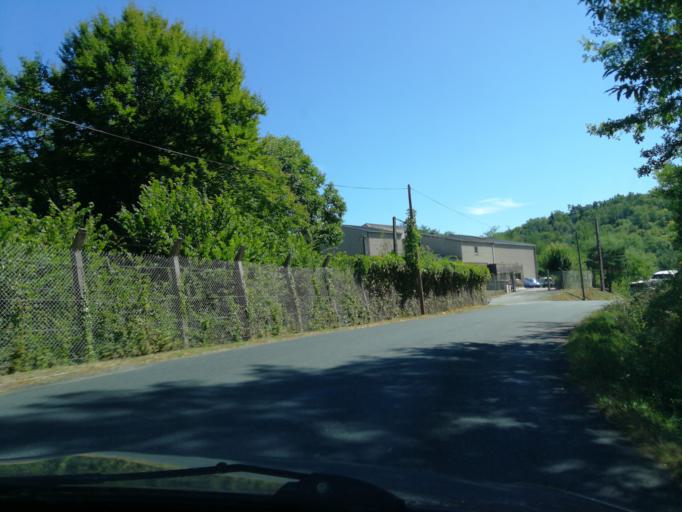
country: FR
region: Limousin
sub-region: Departement de la Correze
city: Argentat
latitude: 45.0912
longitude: 1.9083
